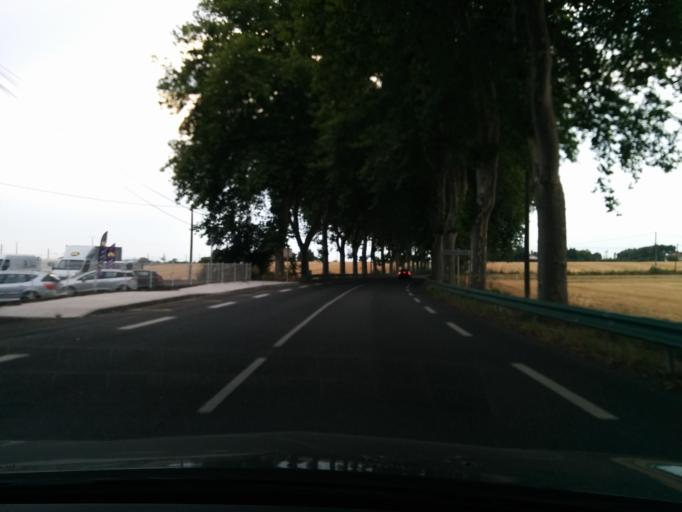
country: FR
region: Midi-Pyrenees
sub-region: Departement de la Haute-Garonne
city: Villefranche-de-Lauragais
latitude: 43.4155
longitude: 1.6958
